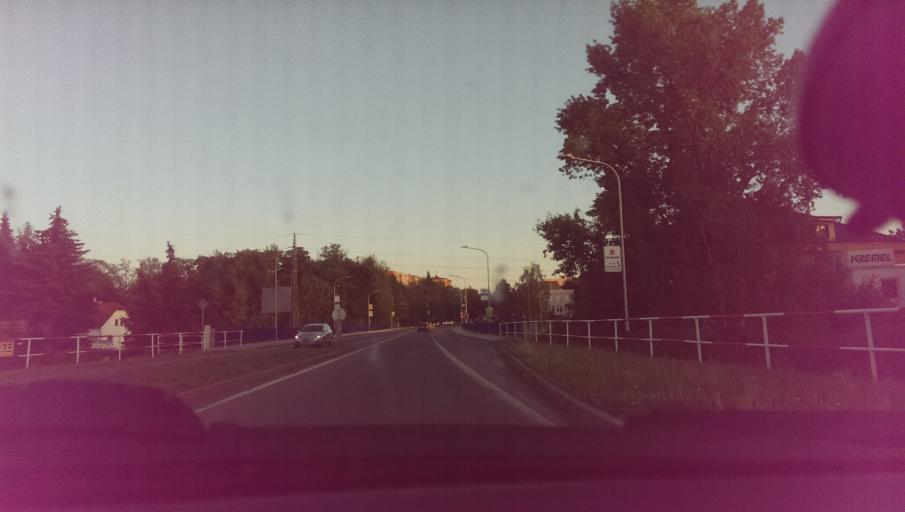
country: CZ
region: Zlin
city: Valasske Mezirici
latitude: 49.4743
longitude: 17.9721
